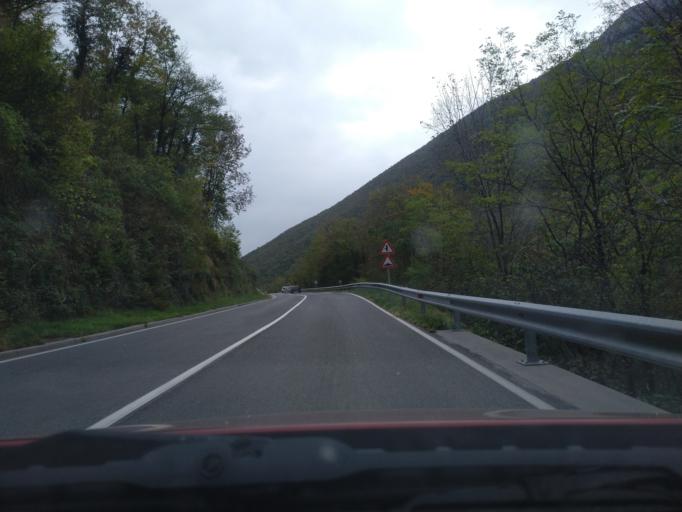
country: SI
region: Nova Gorica
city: Solkan
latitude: 45.9936
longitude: 13.6419
